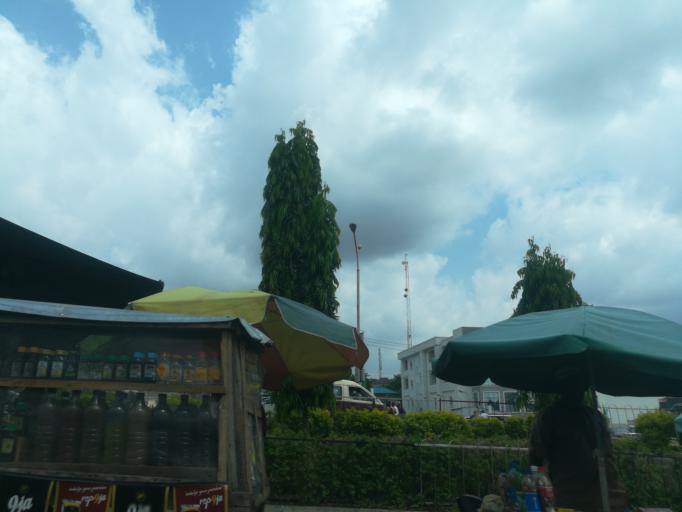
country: NG
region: Oyo
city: Ibadan
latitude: 7.3674
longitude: 3.8606
